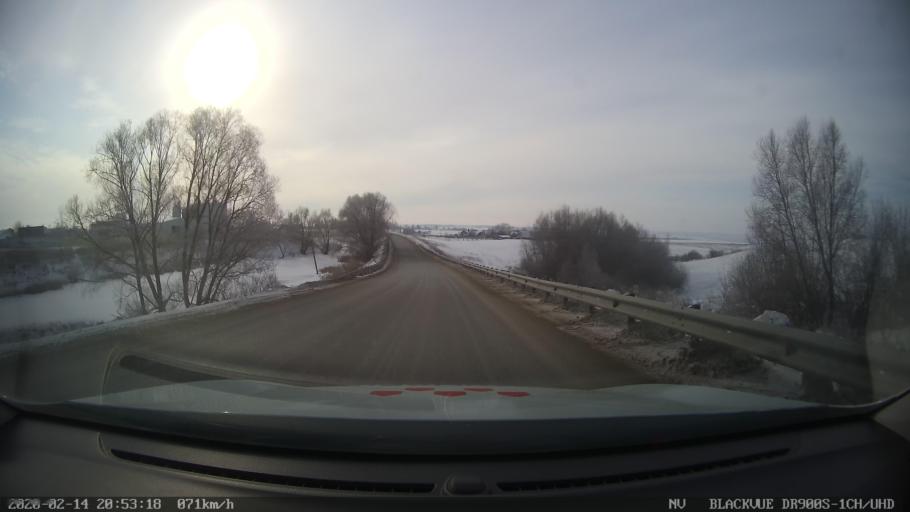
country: RU
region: Tatarstan
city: Kuybyshevskiy Zaton
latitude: 55.1961
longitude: 49.2476
